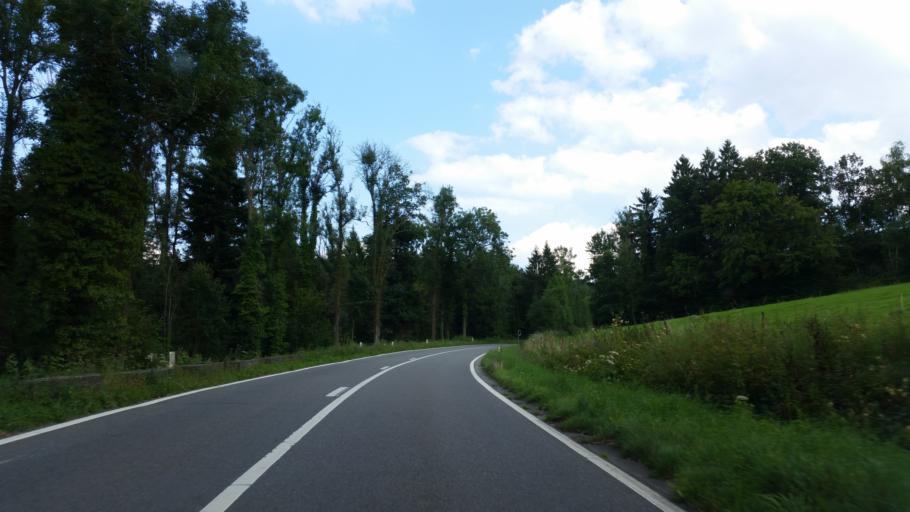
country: BE
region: Wallonia
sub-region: Province de Liege
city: Anthisnes
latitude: 50.4972
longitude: 5.4899
